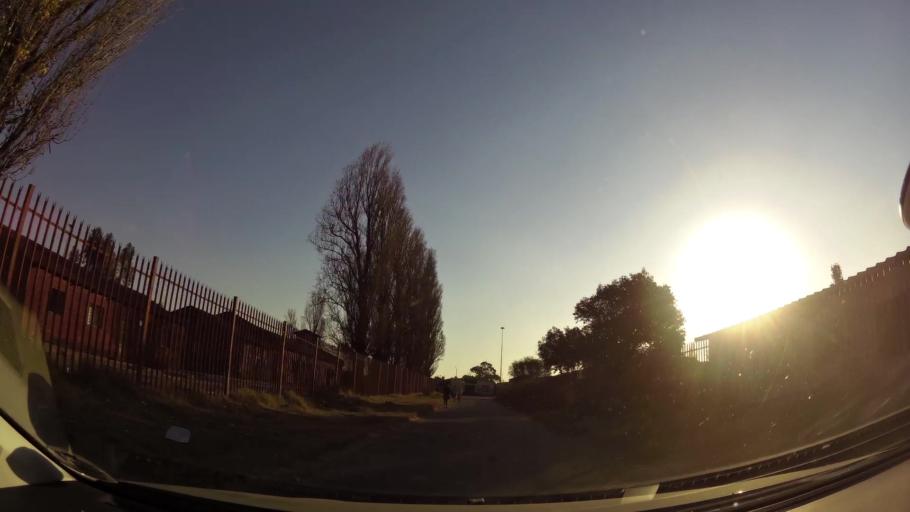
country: ZA
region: Gauteng
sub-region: City of Johannesburg Metropolitan Municipality
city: Soweto
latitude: -26.2532
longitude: 27.8794
